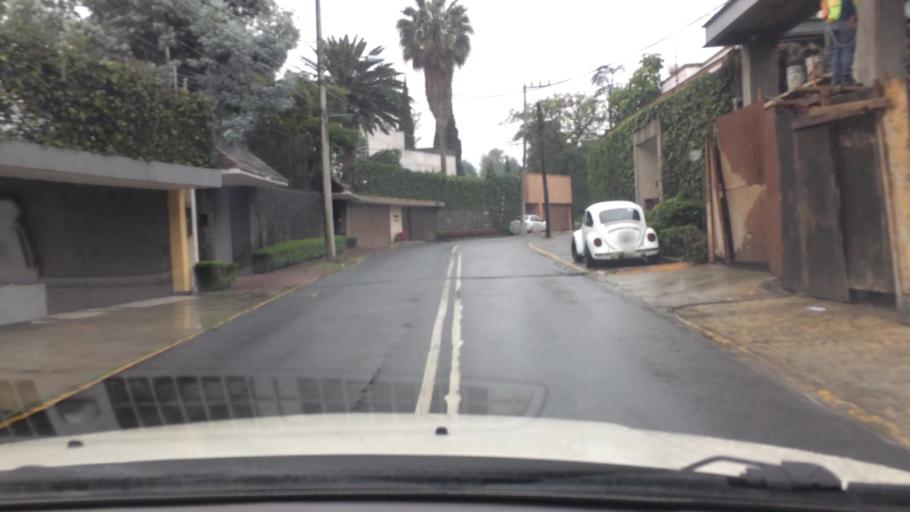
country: MX
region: Mexico City
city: Magdalena Contreras
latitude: 19.3285
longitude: -99.2011
